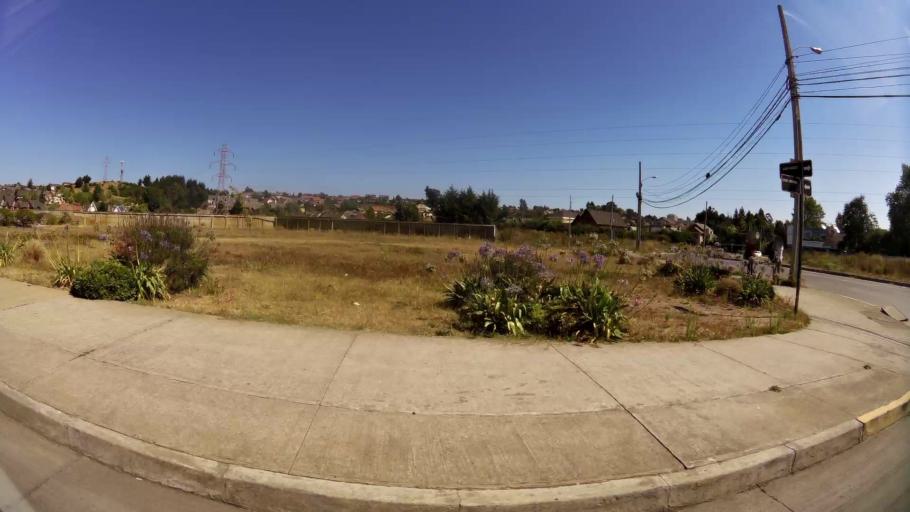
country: CL
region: Biobio
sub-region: Provincia de Concepcion
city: Concepcion
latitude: -36.7880
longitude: -73.0543
